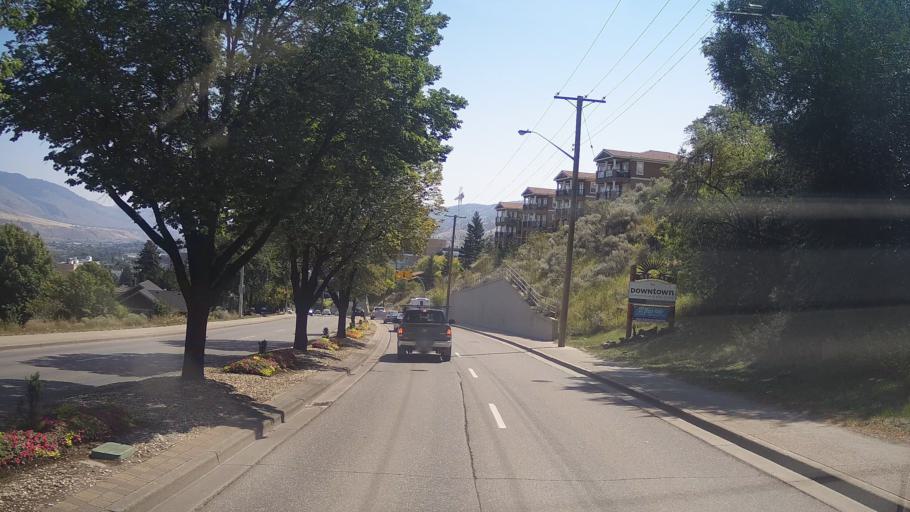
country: CA
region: British Columbia
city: Kamloops
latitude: 50.6717
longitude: -120.3426
